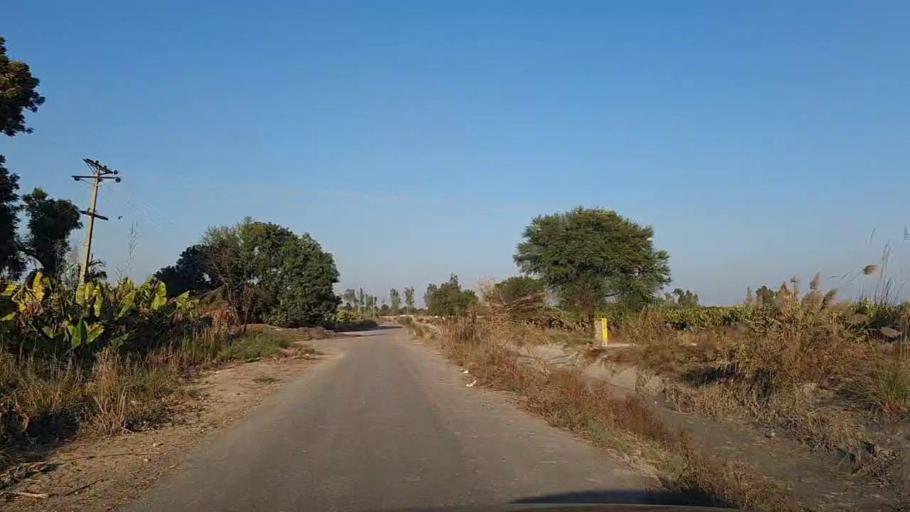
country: PK
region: Sindh
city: Sakrand
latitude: 26.2337
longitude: 68.2788
